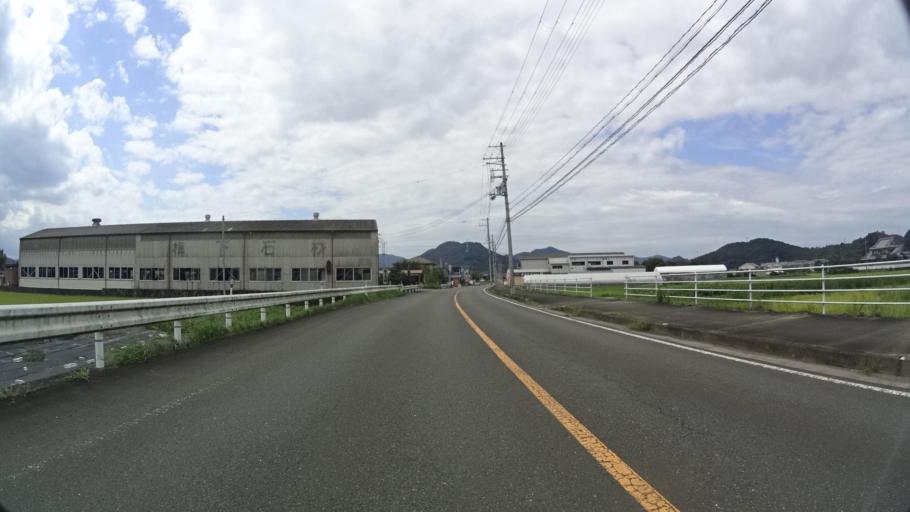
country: JP
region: Kyoto
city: Ayabe
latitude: 35.3097
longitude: 135.2231
